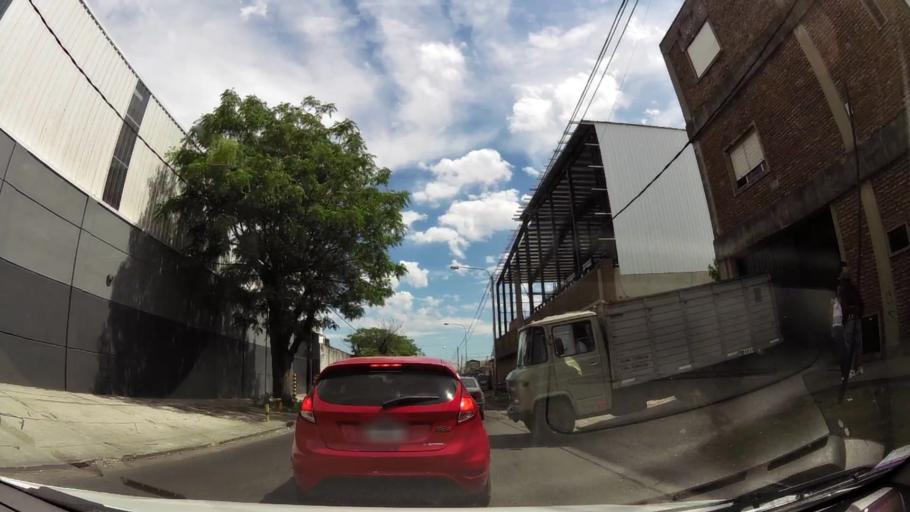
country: AR
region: Buenos Aires
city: San Justo
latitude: -34.6876
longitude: -58.5473
